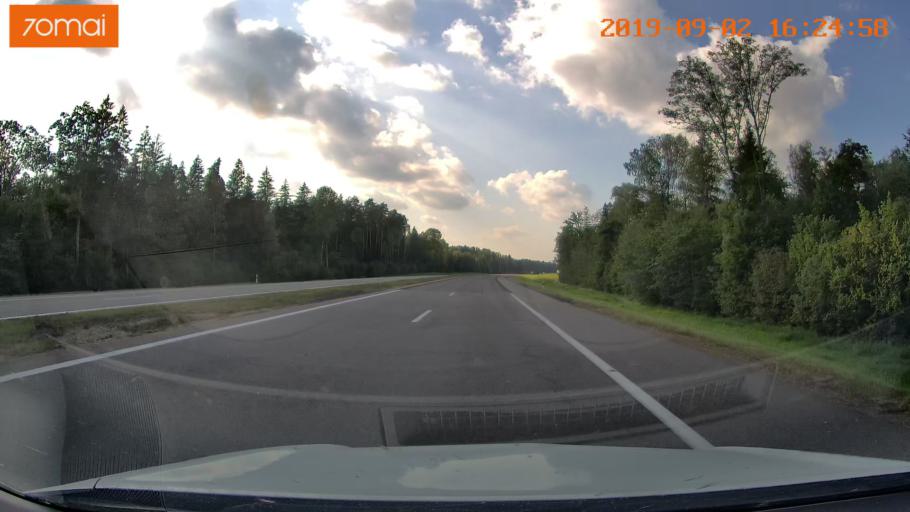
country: BY
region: Minsk
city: Chervyen'
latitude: 53.7508
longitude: 28.2558
